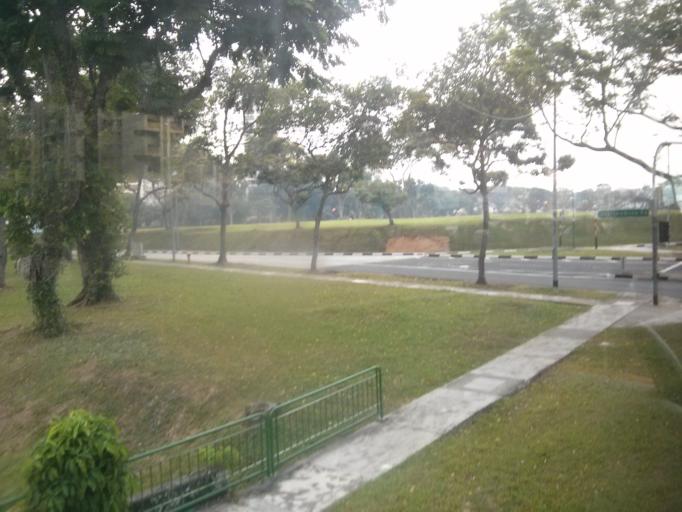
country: SG
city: Singapore
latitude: 1.3480
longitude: 103.8378
